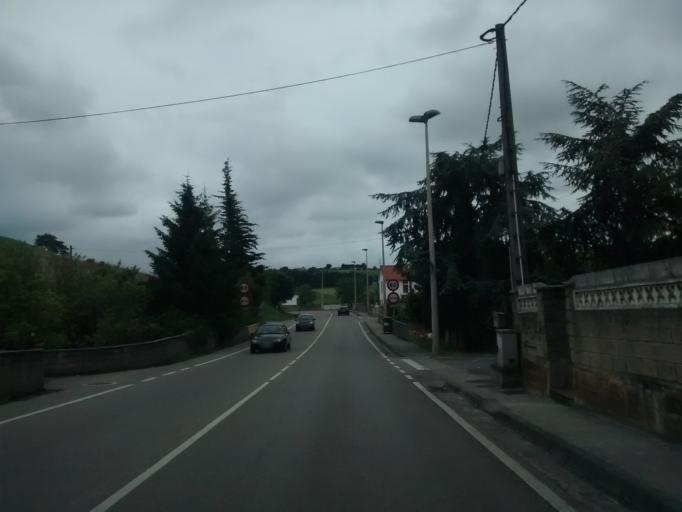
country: ES
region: Cantabria
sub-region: Provincia de Cantabria
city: Polanco
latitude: 43.3938
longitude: -4.0494
